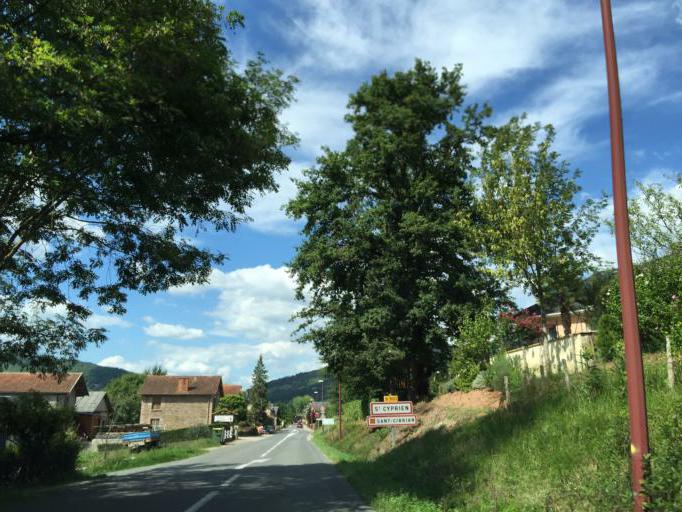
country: FR
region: Midi-Pyrenees
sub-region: Departement de l'Aveyron
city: Saint-Christophe-Vallon
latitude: 44.5424
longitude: 2.4099
